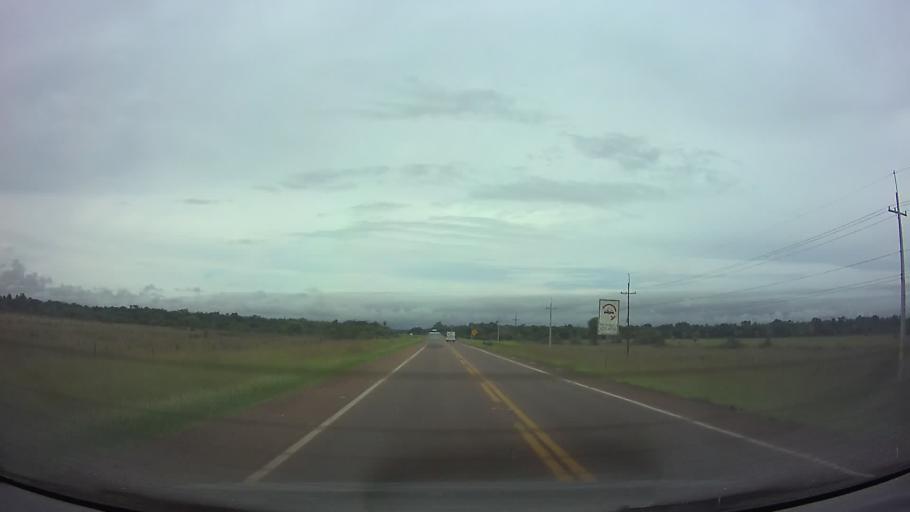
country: PY
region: Paraguari
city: Carapegua
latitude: -25.7307
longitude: -57.2070
